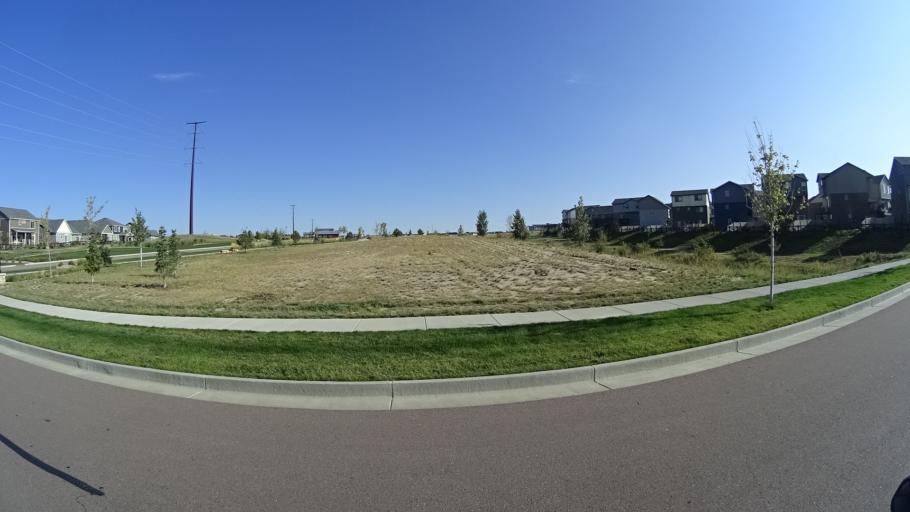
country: US
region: Colorado
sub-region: El Paso County
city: Cimarron Hills
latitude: 38.9282
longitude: -104.6630
